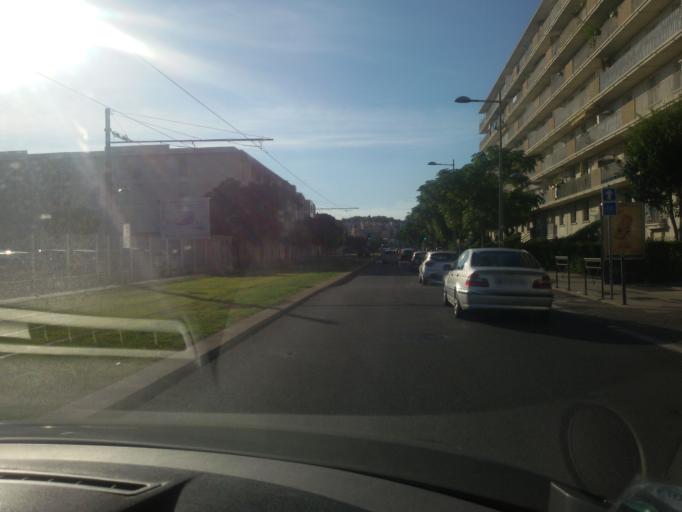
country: FR
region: Languedoc-Roussillon
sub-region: Departement de l'Herault
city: Montpellier
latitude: 43.5911
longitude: 3.8834
